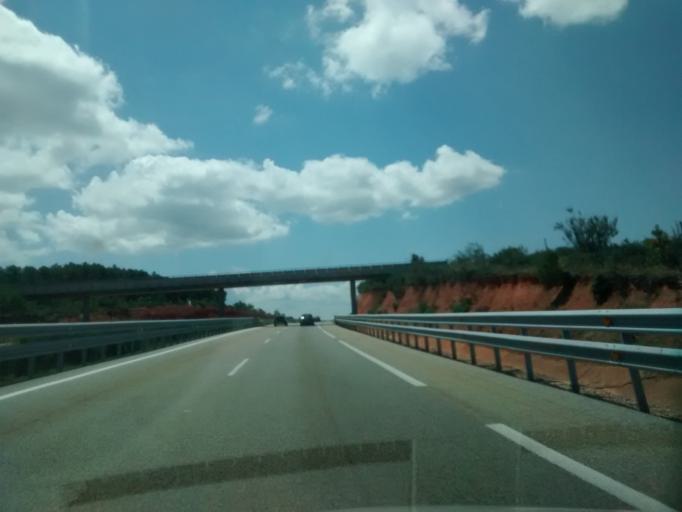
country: ES
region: Castille and Leon
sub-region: Provincia de Leon
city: Brazuelo
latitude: 42.5094
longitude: -6.1170
